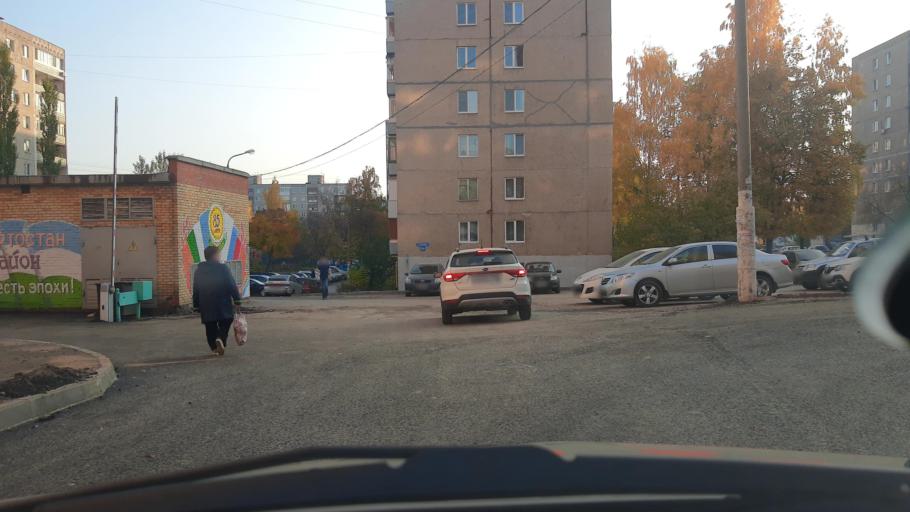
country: RU
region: Bashkortostan
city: Ufa
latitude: 54.7077
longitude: 56.0055
